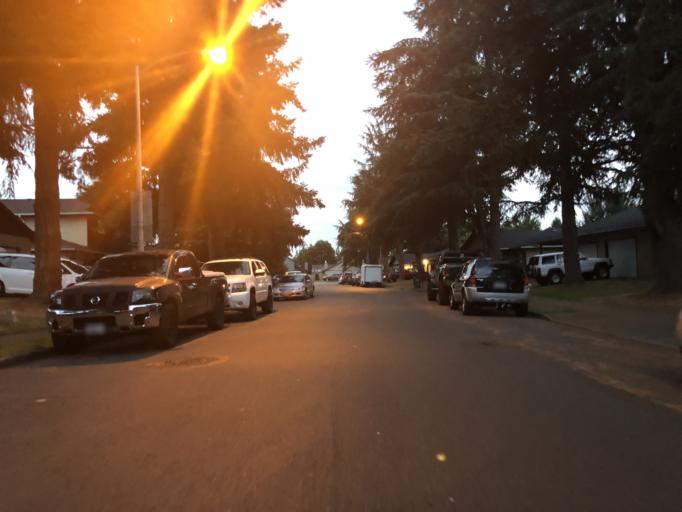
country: US
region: Washington
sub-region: King County
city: Auburn
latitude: 47.3275
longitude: -122.2153
